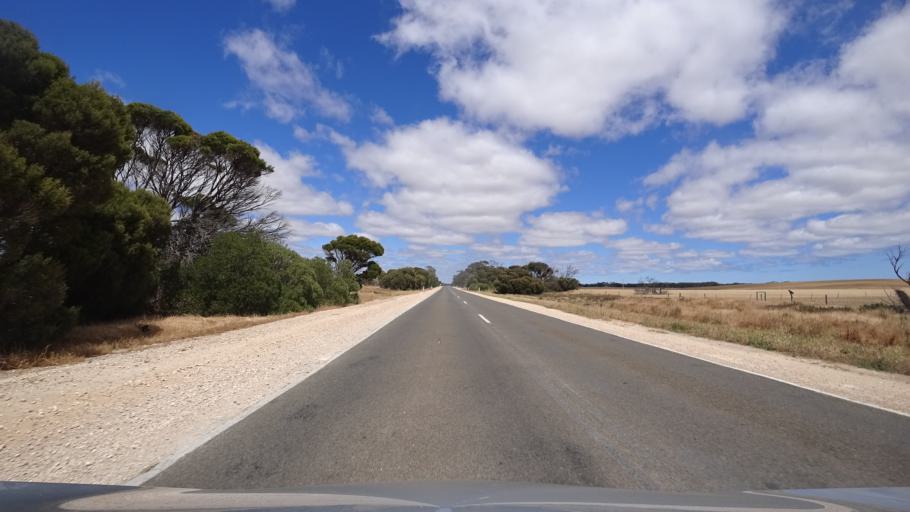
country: AU
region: South Australia
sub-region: Kangaroo Island
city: Kingscote
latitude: -35.6763
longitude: 137.5827
